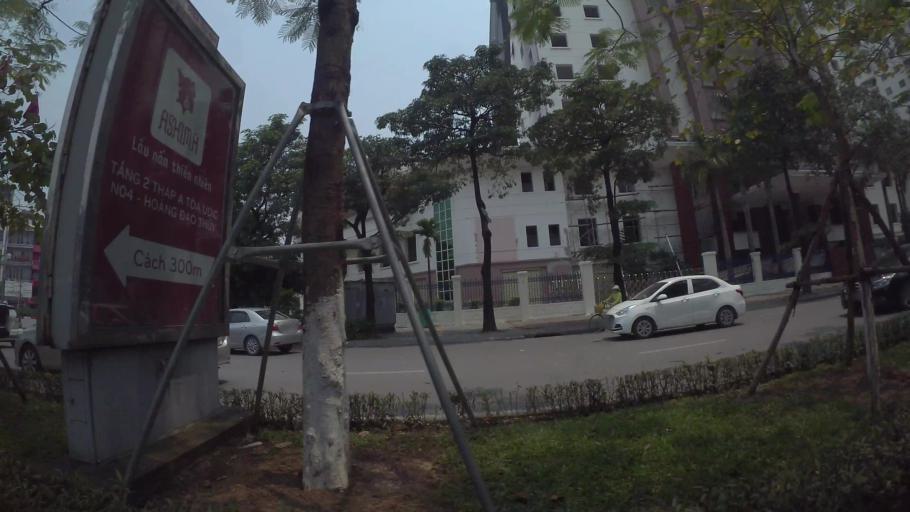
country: VN
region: Ha Noi
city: Thanh Xuan
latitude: 21.0101
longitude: 105.7999
